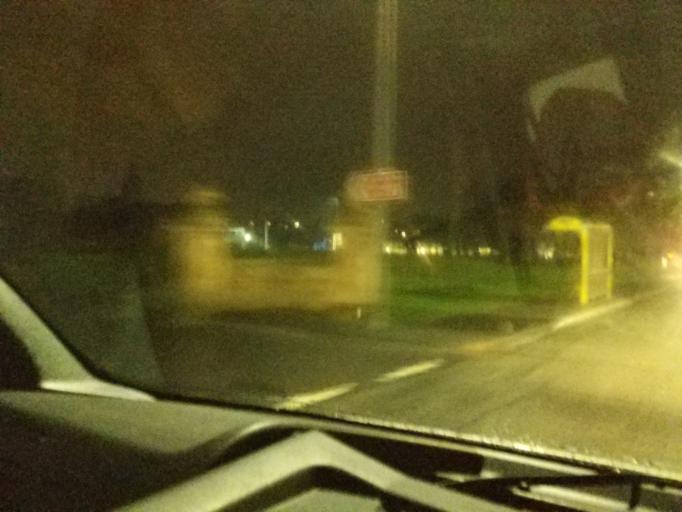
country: GB
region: England
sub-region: St. Helens
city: St Helens
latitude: 53.4635
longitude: -2.7416
